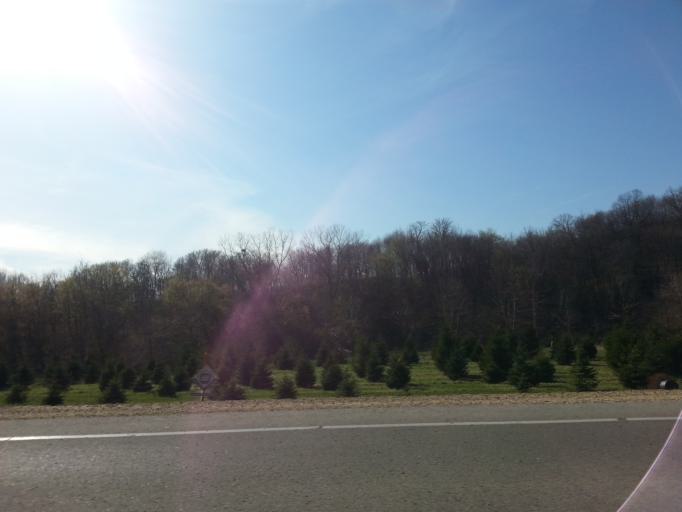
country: US
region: Wisconsin
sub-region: Pierce County
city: Ellsworth
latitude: 44.7629
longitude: -92.4897
